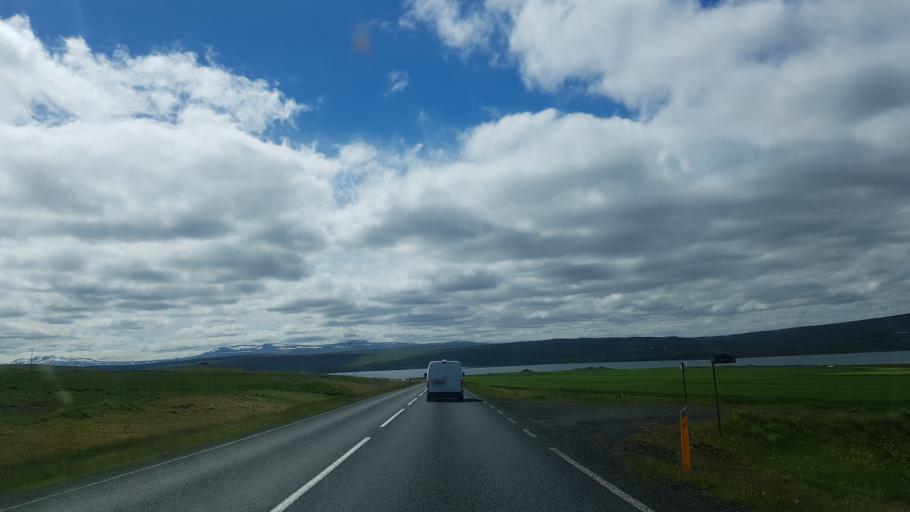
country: IS
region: West
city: Borgarnes
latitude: 65.2716
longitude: -21.0817
